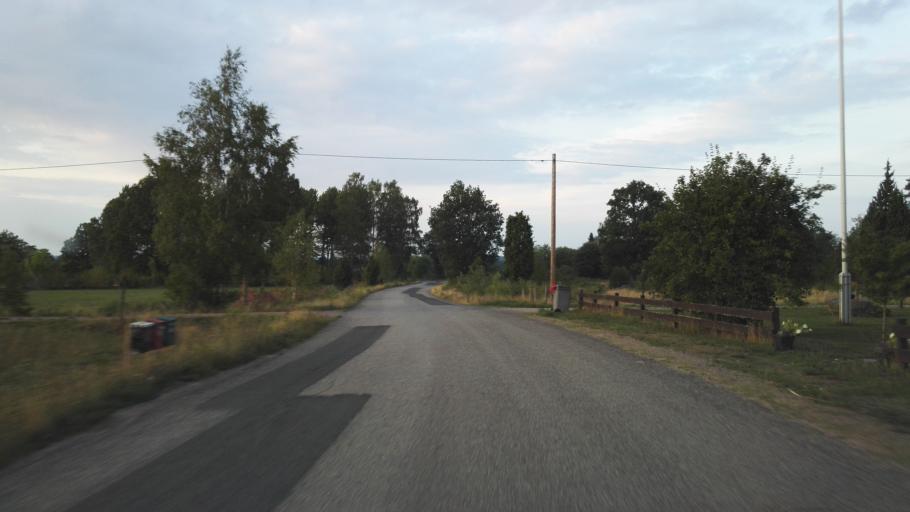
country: SE
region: Joenkoeping
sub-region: Vetlanda Kommun
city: Landsbro
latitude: 57.2540
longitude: 14.8312
